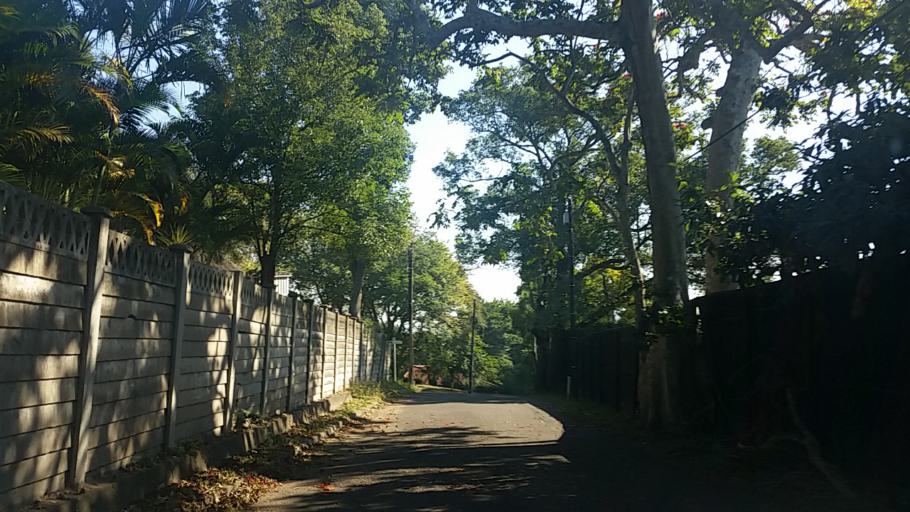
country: ZA
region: KwaZulu-Natal
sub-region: eThekwini Metropolitan Municipality
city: Berea
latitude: -29.8378
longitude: 30.9062
